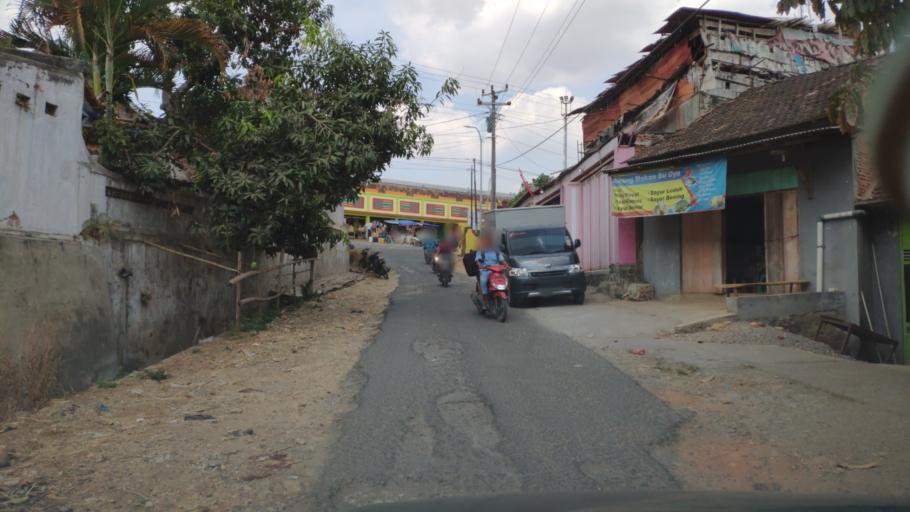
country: ID
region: Central Java
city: Ngapus
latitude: -6.9385
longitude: 111.1783
